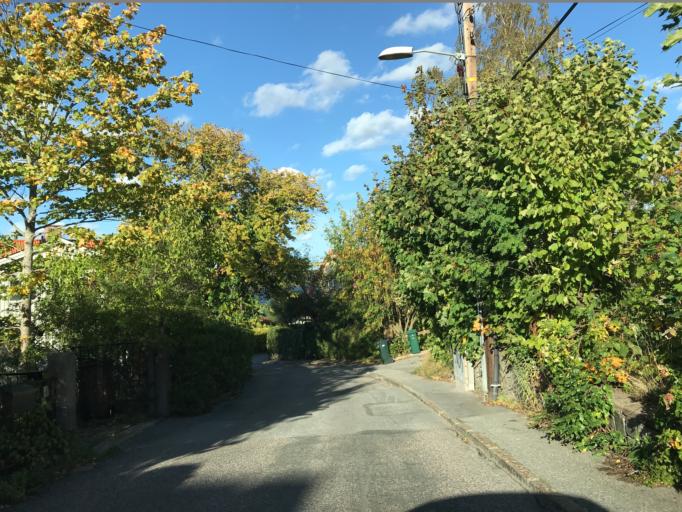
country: SE
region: Stockholm
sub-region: Huddinge Kommun
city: Segeltorp
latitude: 59.3021
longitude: 17.9428
